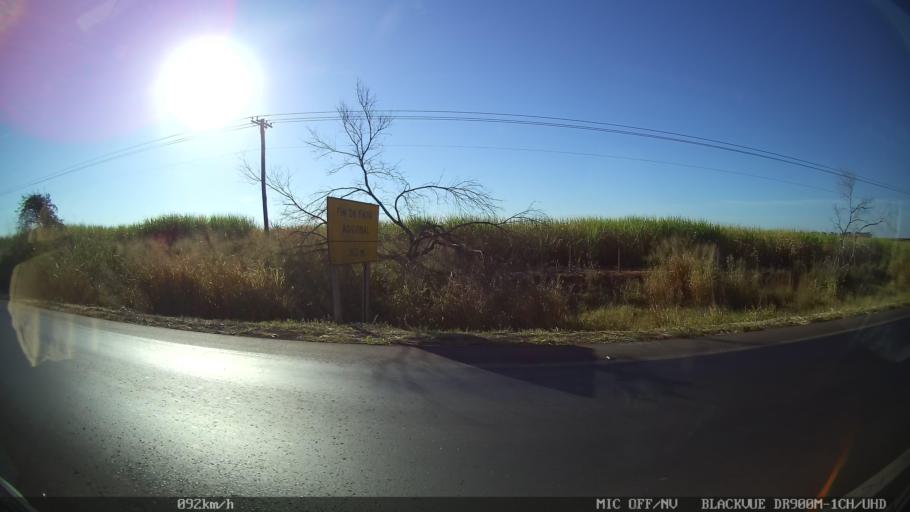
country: BR
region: Sao Paulo
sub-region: Olimpia
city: Olimpia
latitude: -20.7033
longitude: -48.9465
